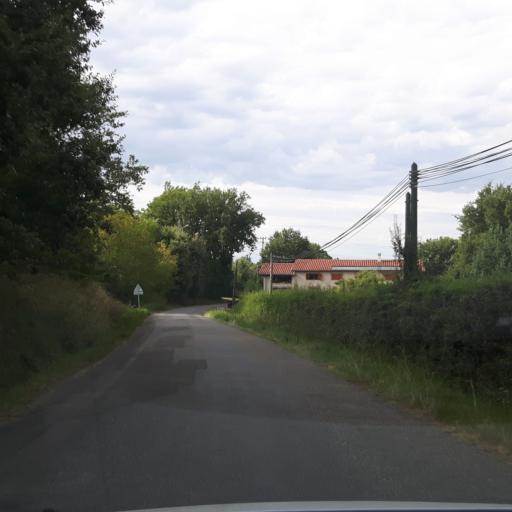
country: FR
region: Midi-Pyrenees
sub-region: Departement de la Haute-Garonne
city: Castelnau-d'Estretefonds
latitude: 43.8050
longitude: 1.3532
